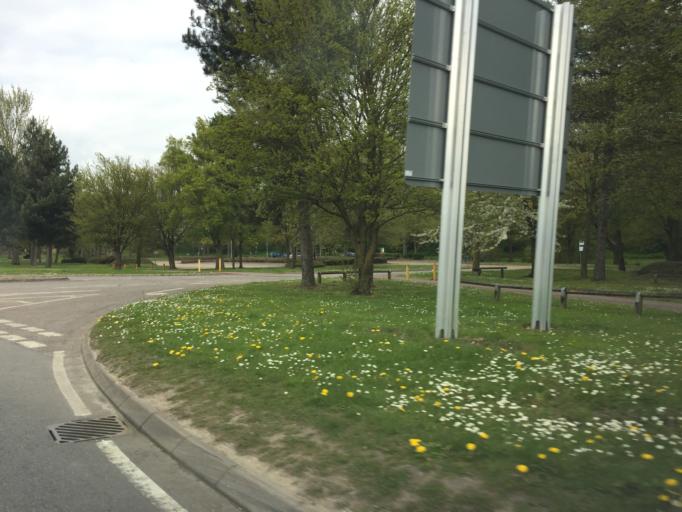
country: GB
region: England
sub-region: Milton Keynes
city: Milton Keynes
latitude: 52.0559
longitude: -0.7284
